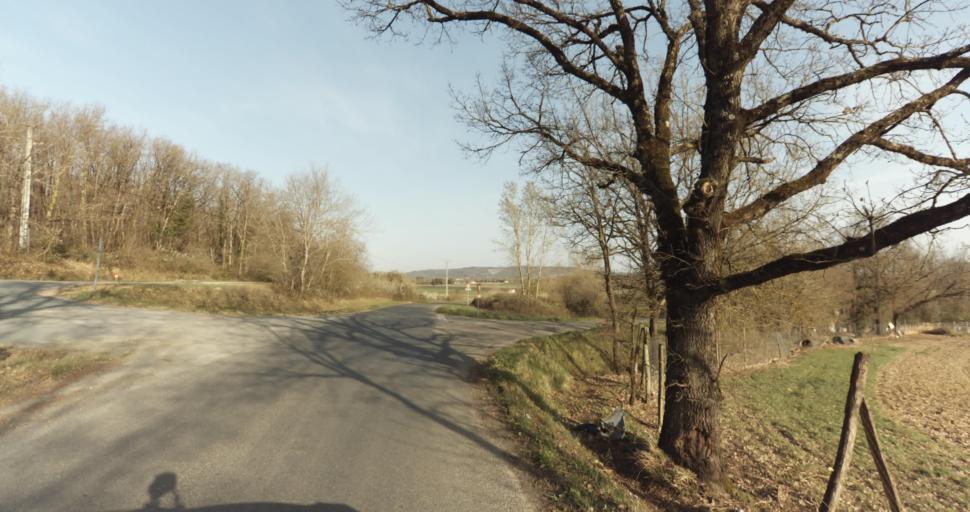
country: FR
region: Midi-Pyrenees
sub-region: Departement du Tarn
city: Saint-Sulpice-la-Pointe
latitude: 43.7503
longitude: 1.6870
